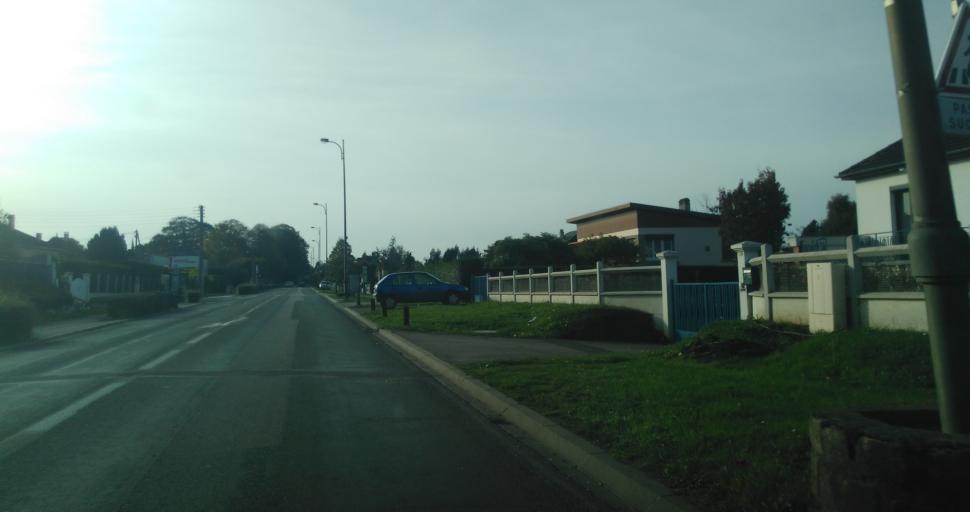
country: FR
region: Haute-Normandie
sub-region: Departement de l'Eure
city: Bourg-Achard
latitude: 49.3569
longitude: 0.8270
